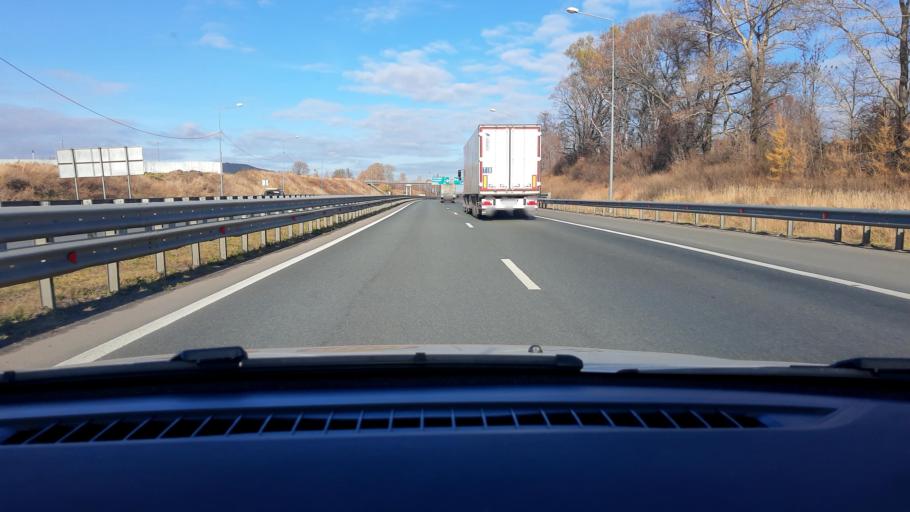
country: RU
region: Nizjnij Novgorod
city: Burevestnik
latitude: 56.1664
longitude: 43.7496
